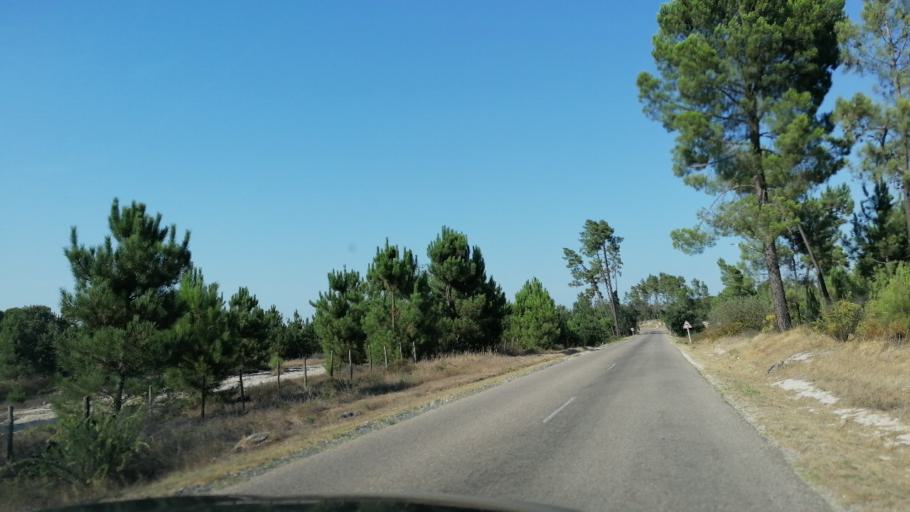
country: PT
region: Santarem
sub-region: Coruche
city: Coruche
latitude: 38.9017
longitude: -8.5297
